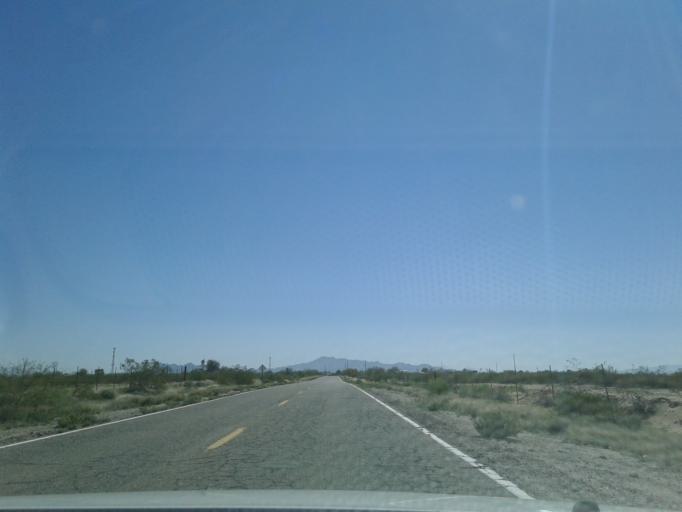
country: US
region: Arizona
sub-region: Pima County
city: Avra Valley
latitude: 32.4538
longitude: -111.3156
